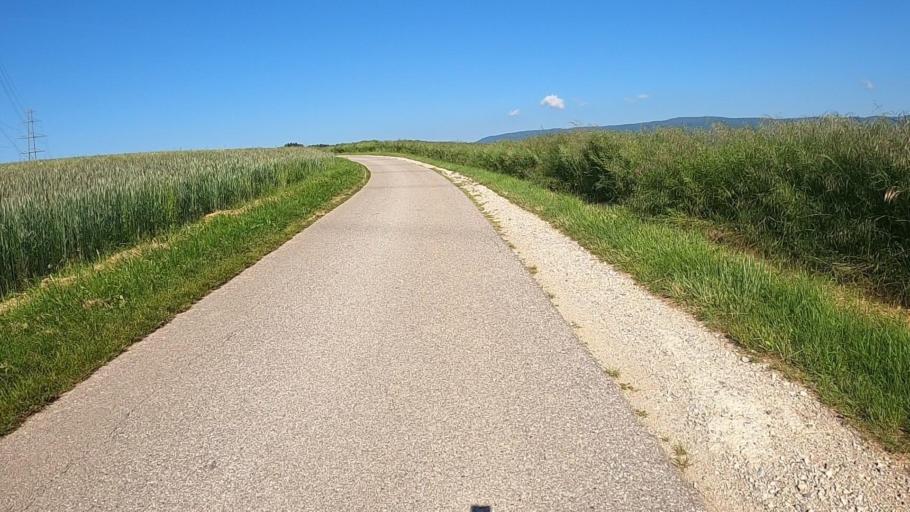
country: CH
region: Vaud
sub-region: Nyon District
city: Rolle
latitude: 46.4833
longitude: 6.3272
